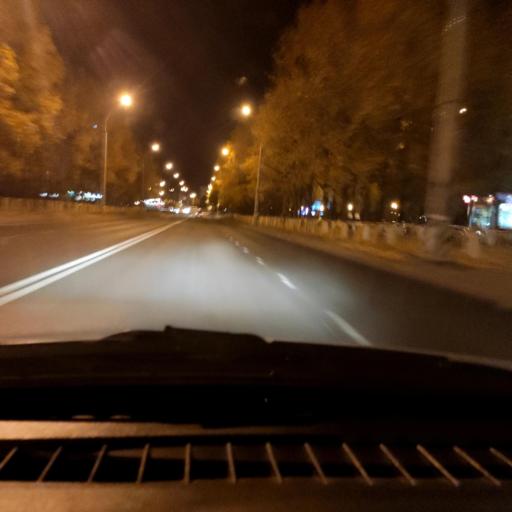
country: RU
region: Samara
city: Tol'yatti
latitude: 53.5360
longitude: 49.3440
